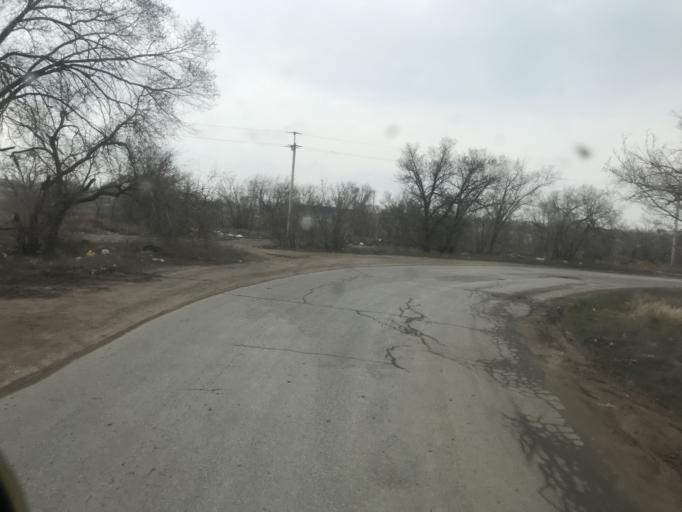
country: RU
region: Volgograd
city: Krasnoslobodsk
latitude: 48.5339
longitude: 44.6061
